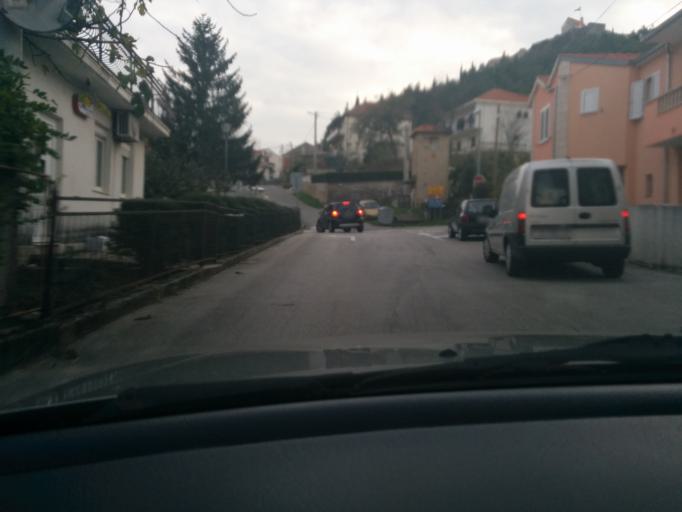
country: HR
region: Splitsko-Dalmatinska
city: Sinj
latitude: 43.7048
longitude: 16.6348
